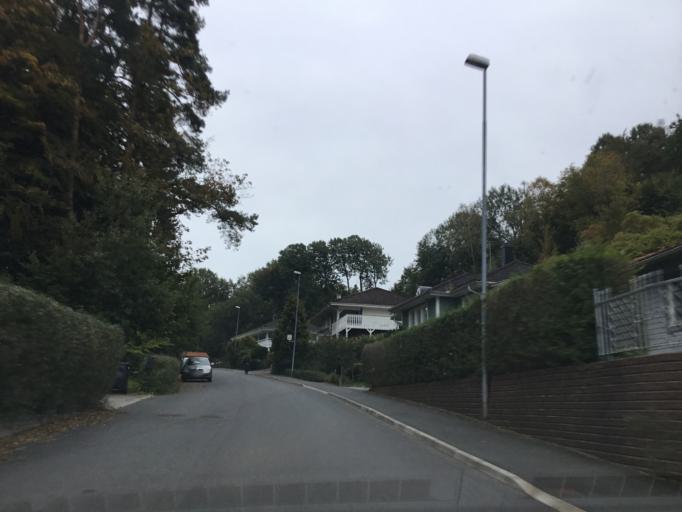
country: SE
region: Vaestra Goetaland
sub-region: Molndal
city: Moelndal
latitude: 57.6545
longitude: 12.0397
